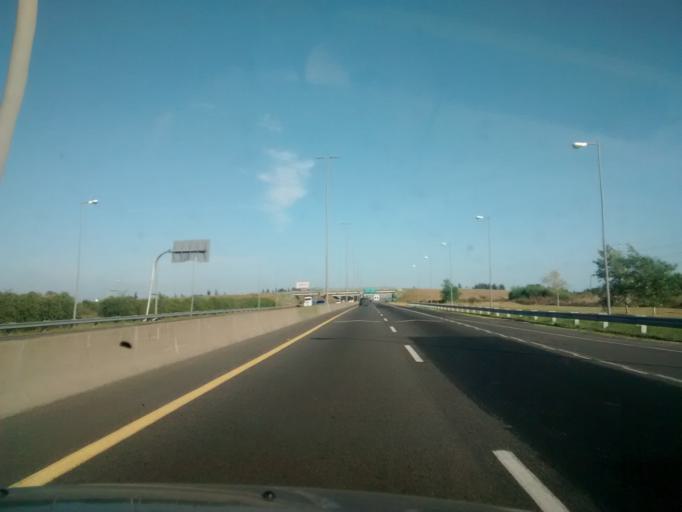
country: AR
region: Buenos Aires
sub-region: Partido de Quilmes
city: Quilmes
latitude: -34.7851
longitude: -58.1483
